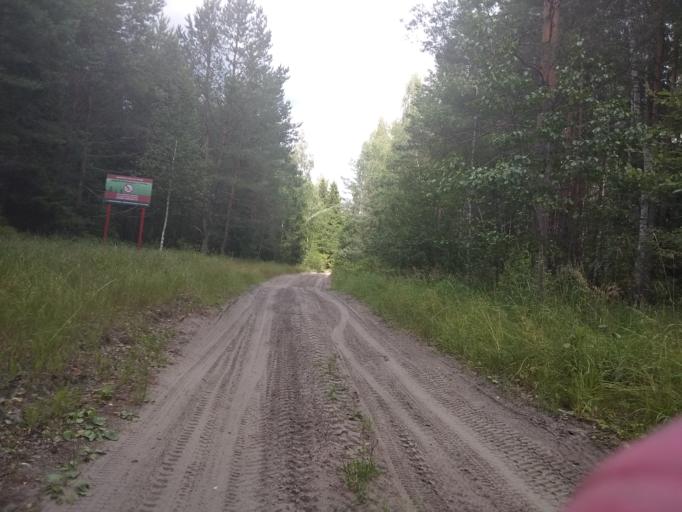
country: RU
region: Moskovskaya
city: Misheronskiy
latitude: 55.7307
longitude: 39.7621
